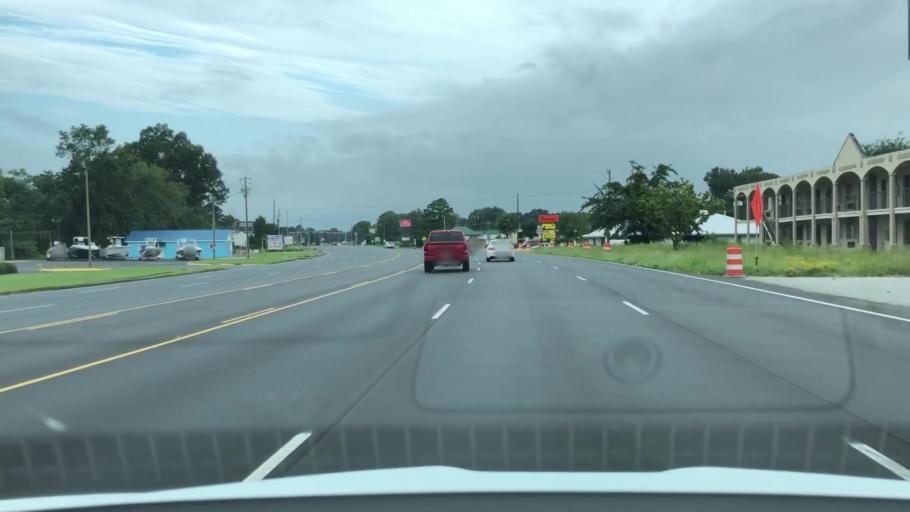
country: US
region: North Carolina
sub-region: Lenoir County
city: Kinston
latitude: 35.2431
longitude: -77.5802
